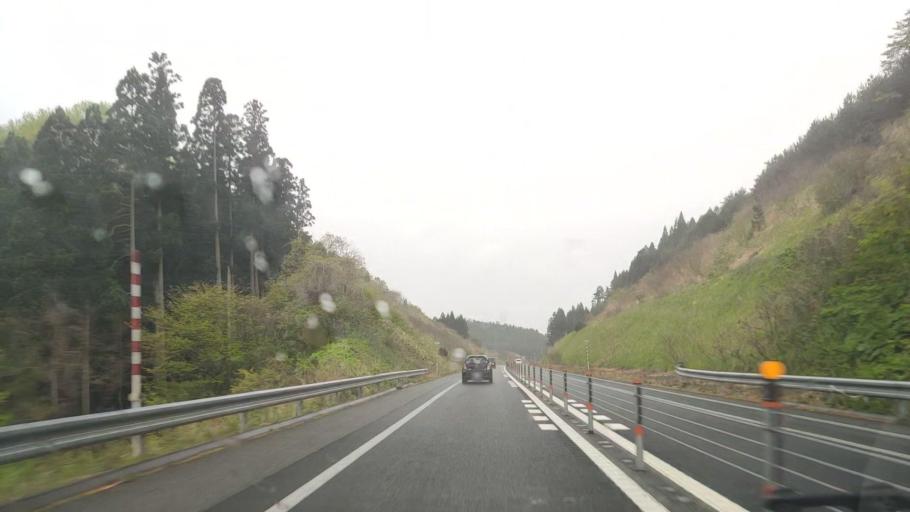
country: JP
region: Akita
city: Noshiromachi
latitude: 40.1959
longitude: 140.1224
